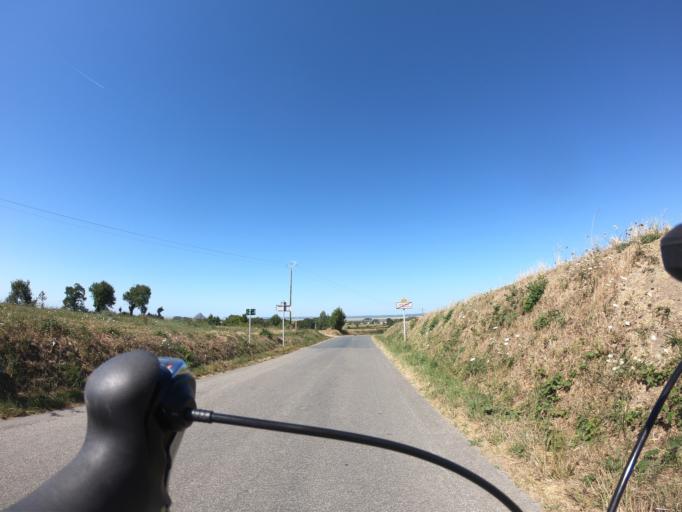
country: FR
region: Lower Normandy
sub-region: Departement de la Manche
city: Pontorson
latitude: 48.5904
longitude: -1.4780
